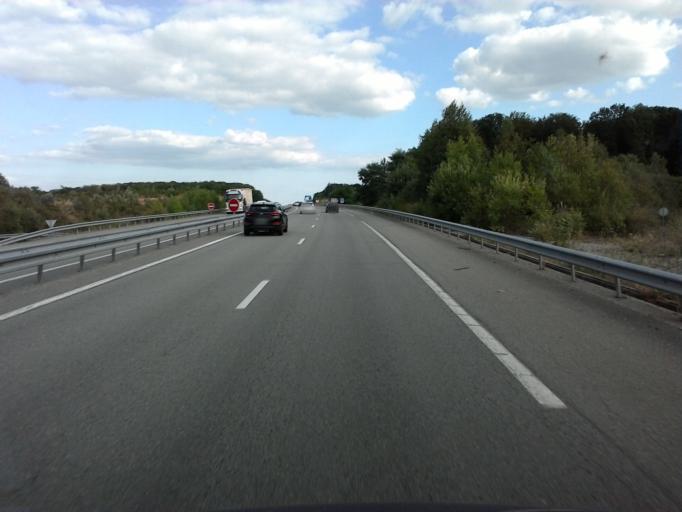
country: FR
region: Franche-Comte
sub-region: Departement de la Haute-Saone
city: Luxeuil-les-Bains
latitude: 47.8501
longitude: 6.3859
